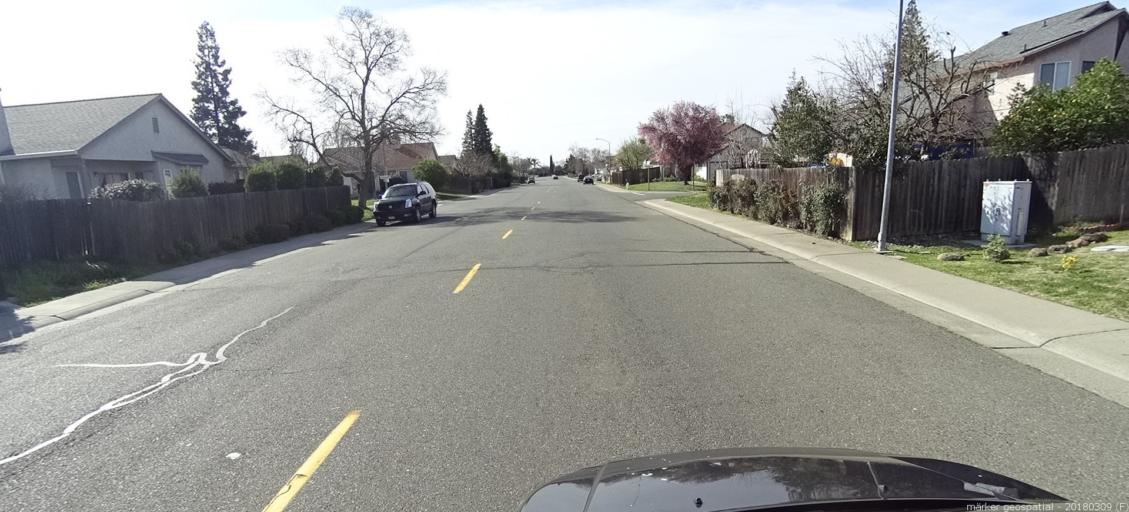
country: US
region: California
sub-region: Sacramento County
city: Florin
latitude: 38.4584
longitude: -121.3991
